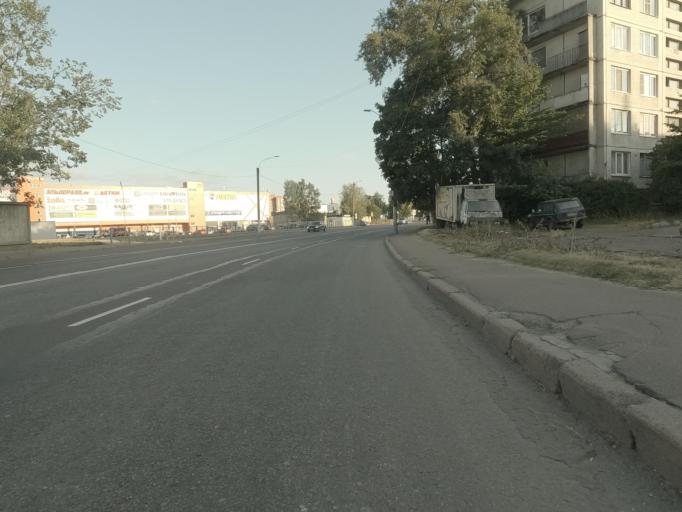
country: RU
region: Leningrad
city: Vyborg
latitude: 60.7090
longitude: 28.7709
